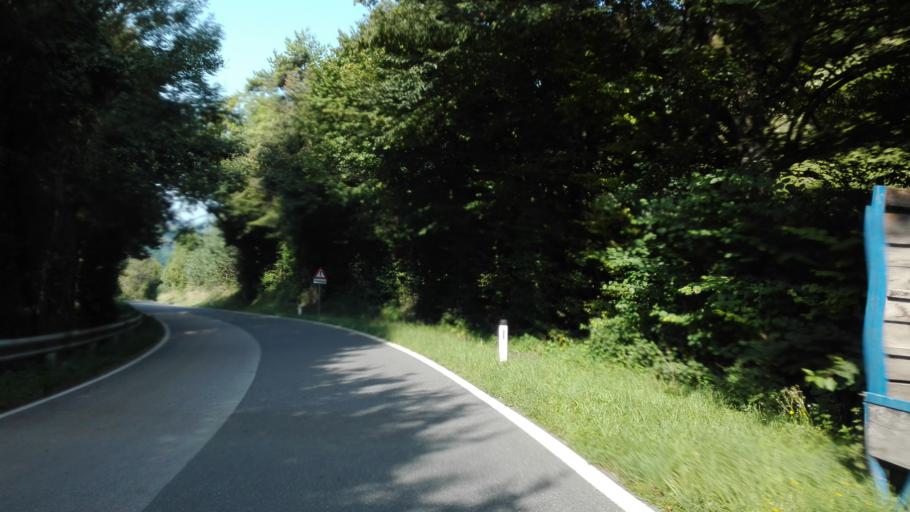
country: AT
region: Lower Austria
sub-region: Politischer Bezirk Sankt Polten
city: Rabenstein an der Pielach
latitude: 48.0342
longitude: 15.4874
